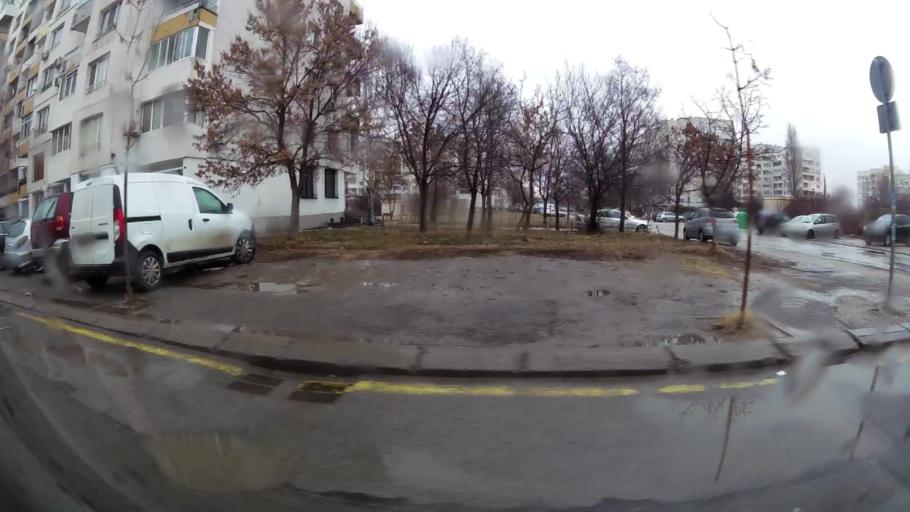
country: BG
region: Sofia-Capital
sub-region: Stolichna Obshtina
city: Sofia
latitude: 42.6404
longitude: 23.4145
